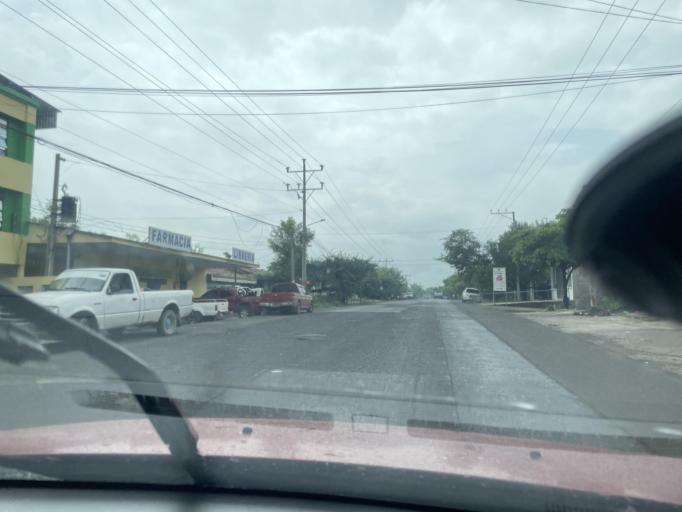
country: SV
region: La Union
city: Santa Rosa de Lima
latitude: 13.6189
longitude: -87.9008
